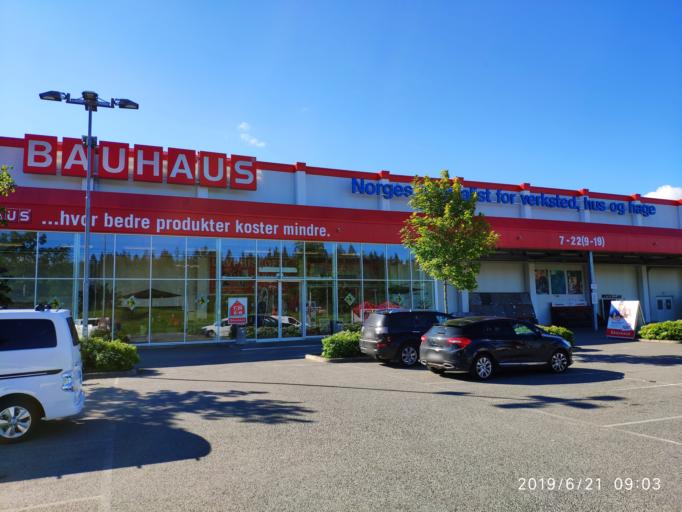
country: NO
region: Buskerud
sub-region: Lier
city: Tranby
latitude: 59.8085
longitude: 10.2957
